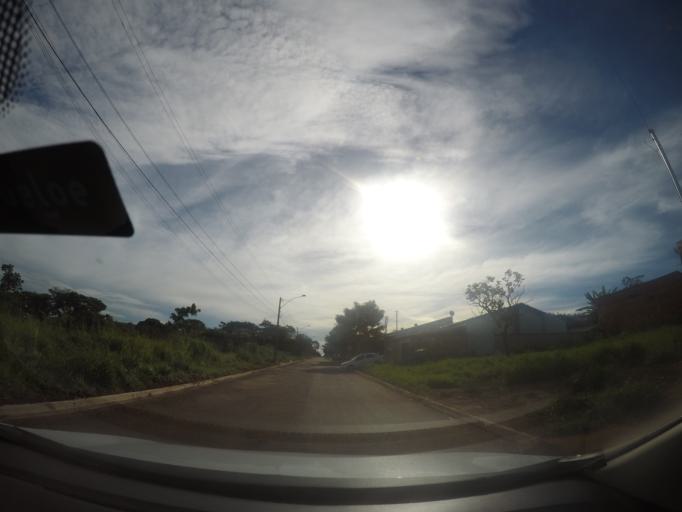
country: BR
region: Goias
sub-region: Goiania
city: Goiania
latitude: -16.6319
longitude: -49.3548
